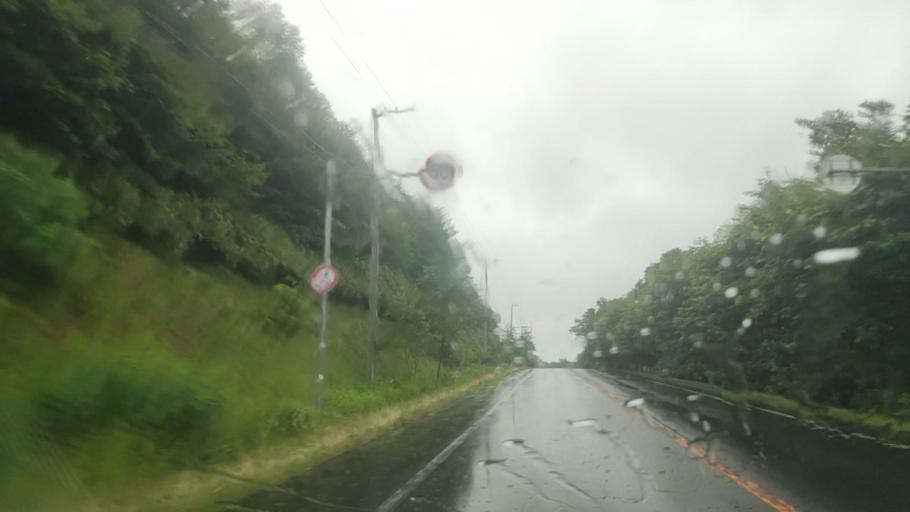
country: JP
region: Hokkaido
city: Muroran
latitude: 42.5036
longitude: 141.1097
